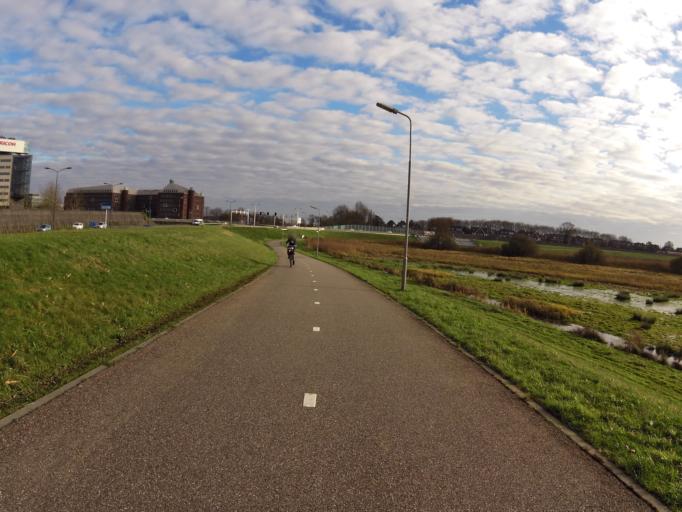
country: NL
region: North Brabant
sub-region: Gemeente 's-Hertogenbosch
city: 's-Hertogenbosch
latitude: 51.6824
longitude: 5.2858
